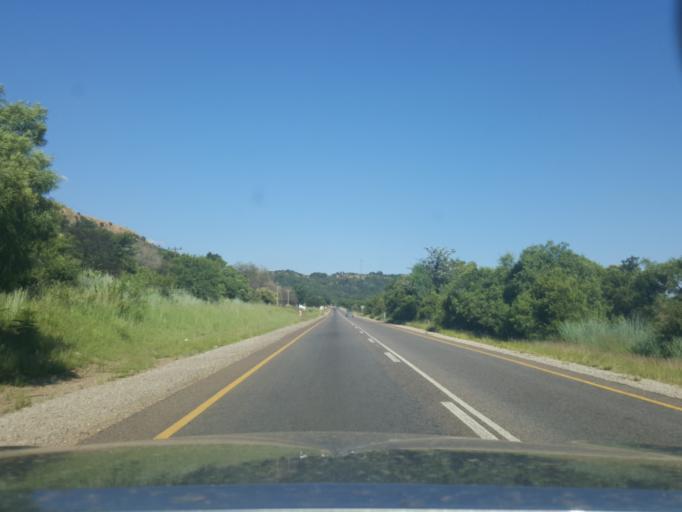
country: ZA
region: Gauteng
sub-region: City of Tshwane Metropolitan Municipality
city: Cullinan
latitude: -25.7775
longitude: 28.4720
